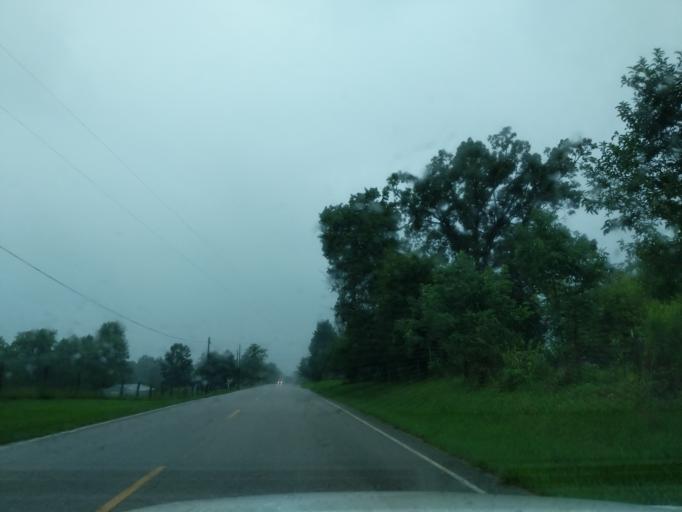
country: US
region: Kentucky
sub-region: Barren County
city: Cave City
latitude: 37.1304
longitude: -86.0486
